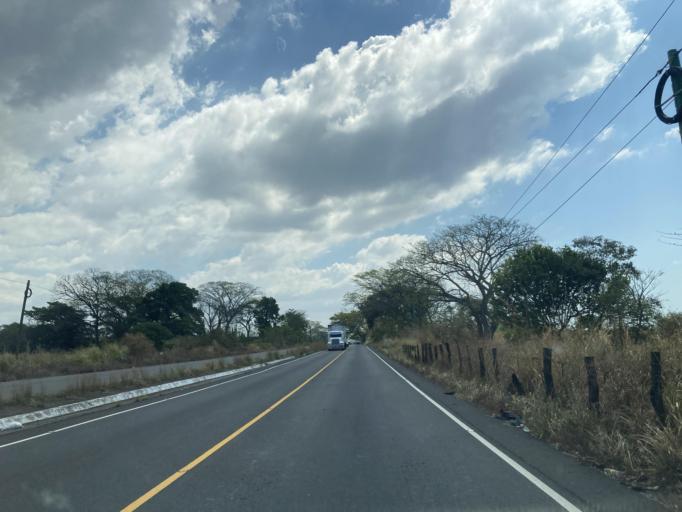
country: GT
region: Santa Rosa
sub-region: Municipio de Taxisco
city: Taxisco
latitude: 14.0960
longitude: -90.5290
